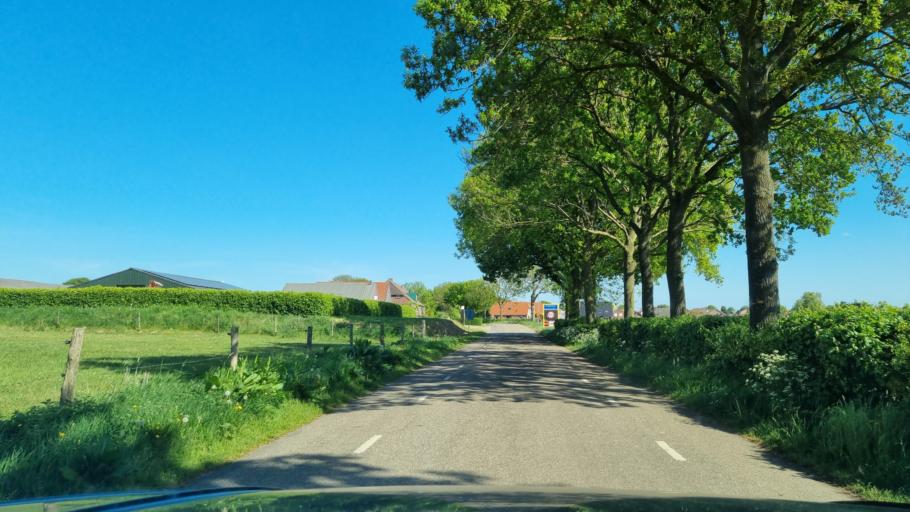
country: NL
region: North Brabant
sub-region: Gemeente Cuijk
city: Cuijk
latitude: 51.7321
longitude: 5.9065
